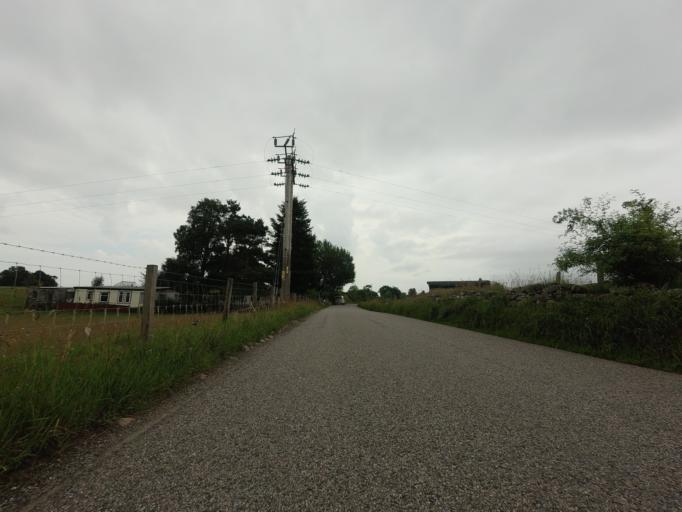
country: GB
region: Scotland
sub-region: Highland
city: Evanton
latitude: 57.8861
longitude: -4.3833
